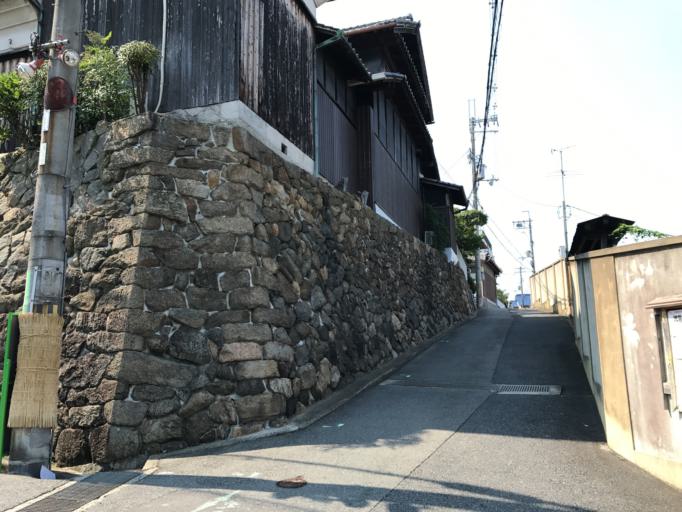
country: JP
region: Osaka
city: Kashihara
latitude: 34.6072
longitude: 135.6351
